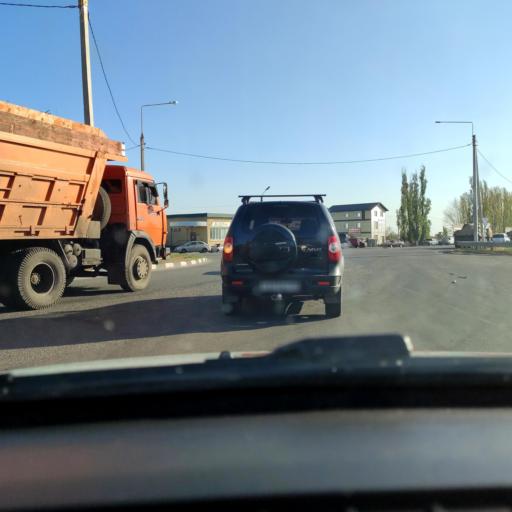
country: RU
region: Voronezj
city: Semiluki
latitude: 51.7258
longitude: 39.0348
